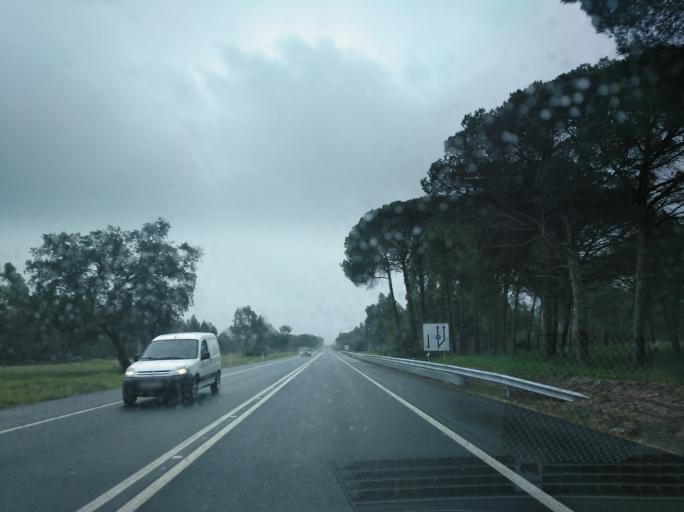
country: PT
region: Setubal
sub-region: Alcacer do Sal
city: Alcacer do Sal
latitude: 38.3257
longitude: -8.5245
